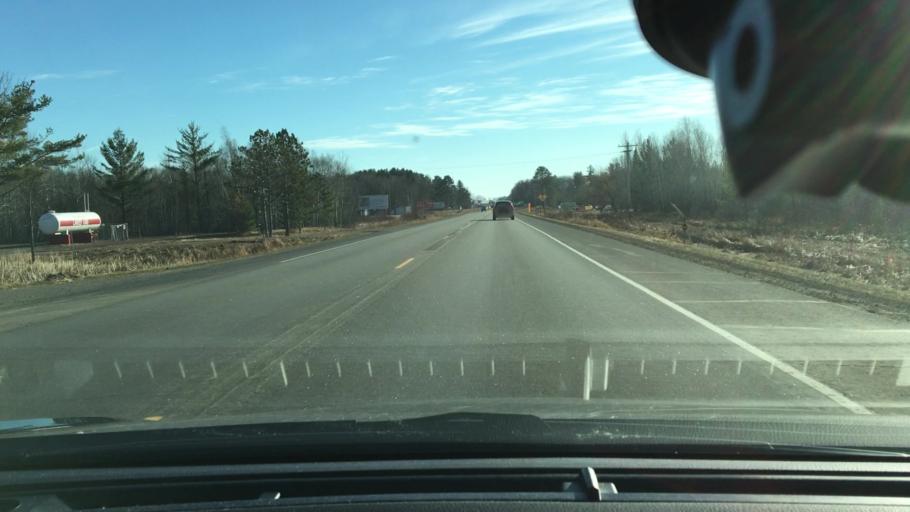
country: US
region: Minnesota
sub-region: Mille Lacs County
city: Vineland
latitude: 46.3049
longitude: -93.8305
